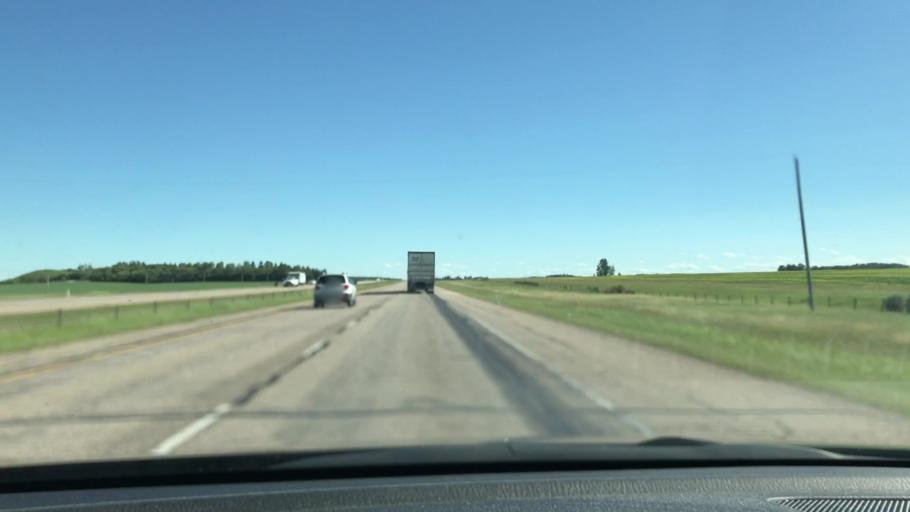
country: CA
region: Alberta
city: Olds
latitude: 51.8651
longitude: -114.0257
